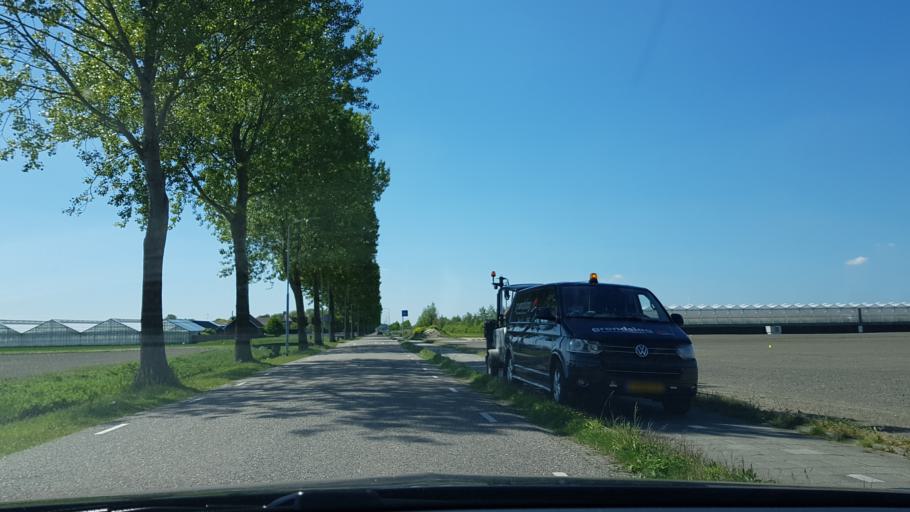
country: NL
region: South Holland
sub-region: Gemeente Kaag en Braassem
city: Leimuiden
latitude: 52.2461
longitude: 4.6865
